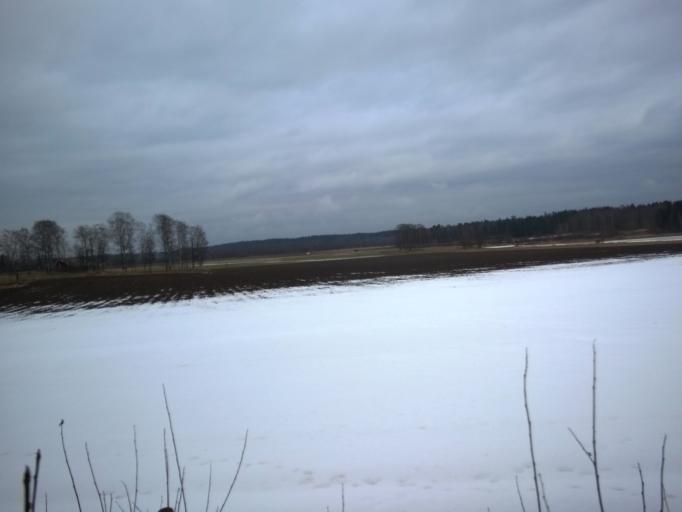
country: FI
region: Uusimaa
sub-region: Helsinki
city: Vantaa
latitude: 60.2161
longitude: 25.0123
